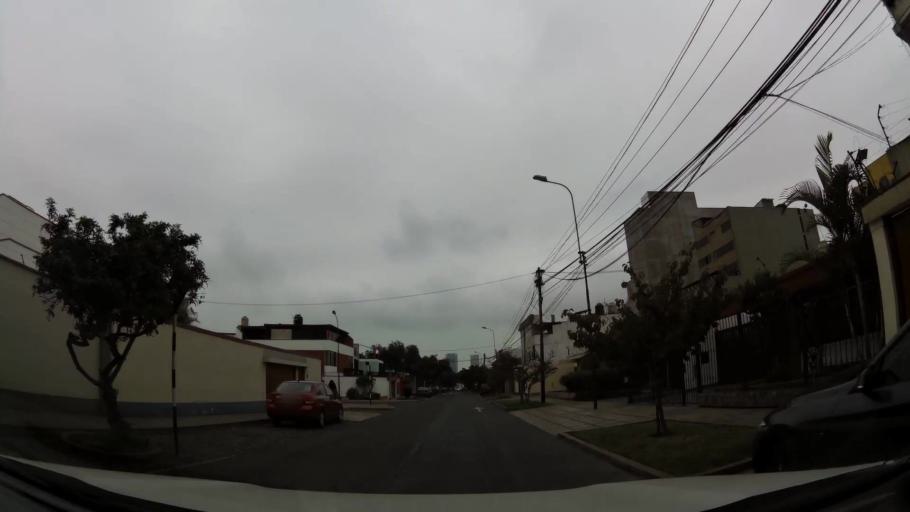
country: PE
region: Lima
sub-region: Lima
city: San Luis
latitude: -12.0899
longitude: -77.0101
